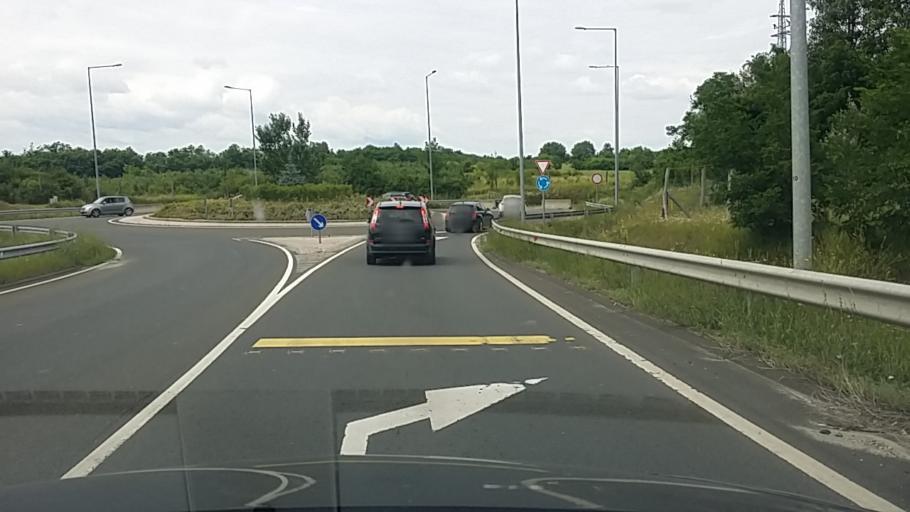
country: HU
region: Pest
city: Szada
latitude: 47.6151
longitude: 19.3257
